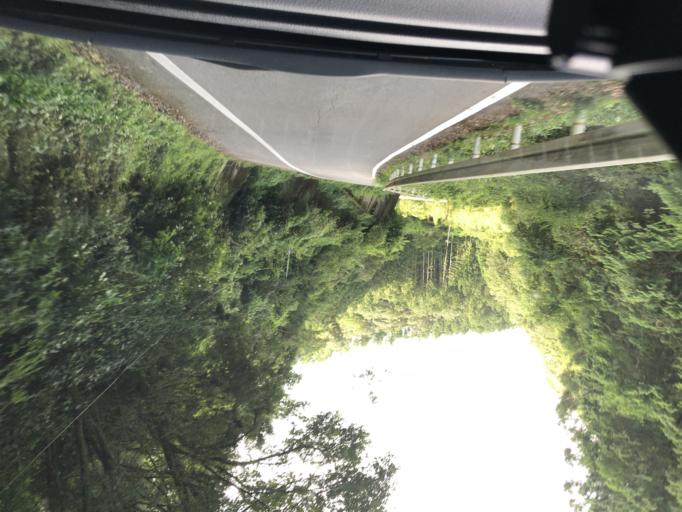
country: JP
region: Kochi
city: Kochi-shi
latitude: 33.6148
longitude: 133.4977
